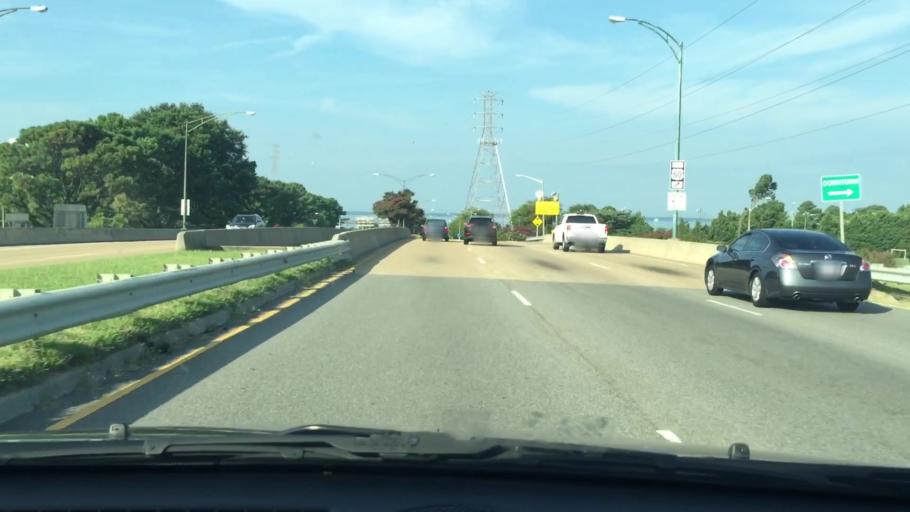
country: US
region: Virginia
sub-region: City of Newport News
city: Newport News
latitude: 37.0177
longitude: -76.4497
